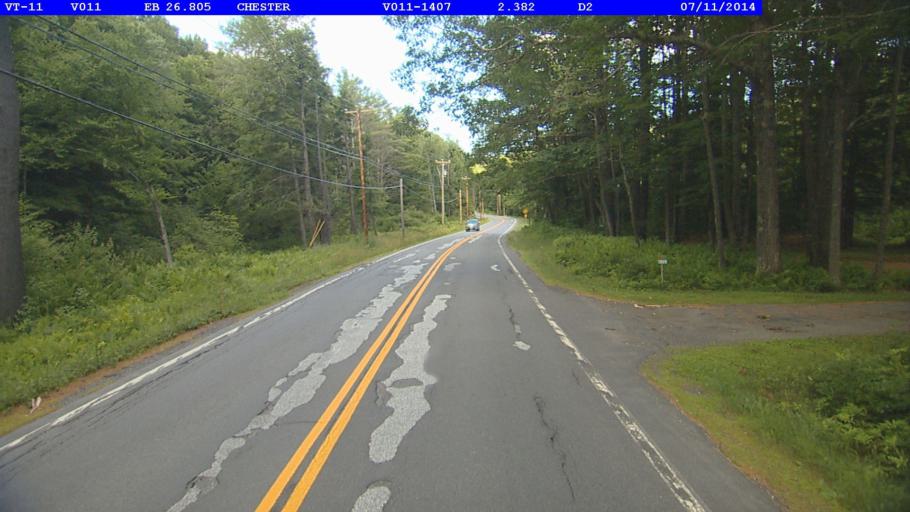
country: US
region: Vermont
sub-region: Windsor County
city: Chester
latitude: 43.2624
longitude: -72.6406
